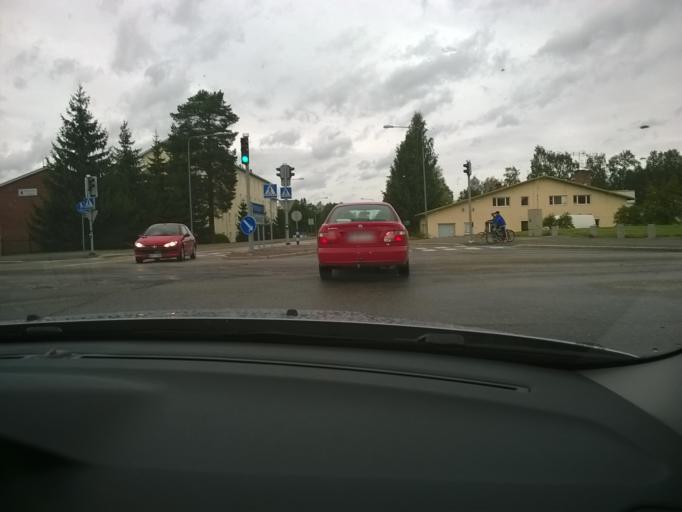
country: FI
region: Kainuu
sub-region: Kehys-Kainuu
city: Kuhmo
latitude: 64.1236
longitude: 29.5106
